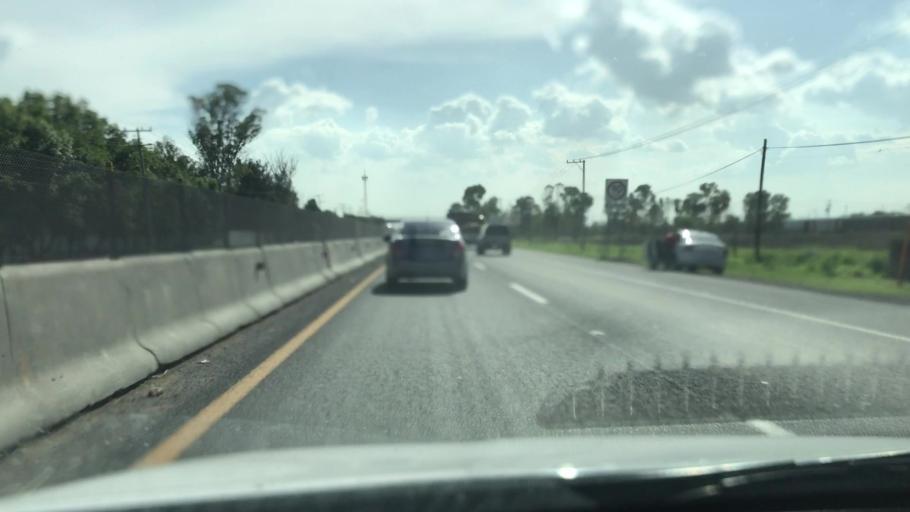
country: MX
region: Guanajuato
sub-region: Cortazar
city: Colonia la Calzada (La Olla)
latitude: 20.5104
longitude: -100.9656
